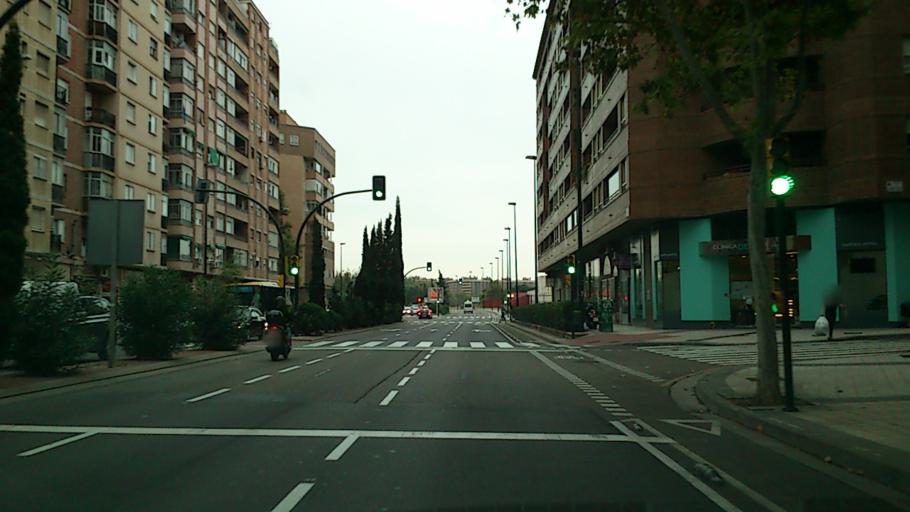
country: ES
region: Aragon
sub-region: Provincia de Zaragoza
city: Zaragoza
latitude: 41.6616
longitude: -0.8647
